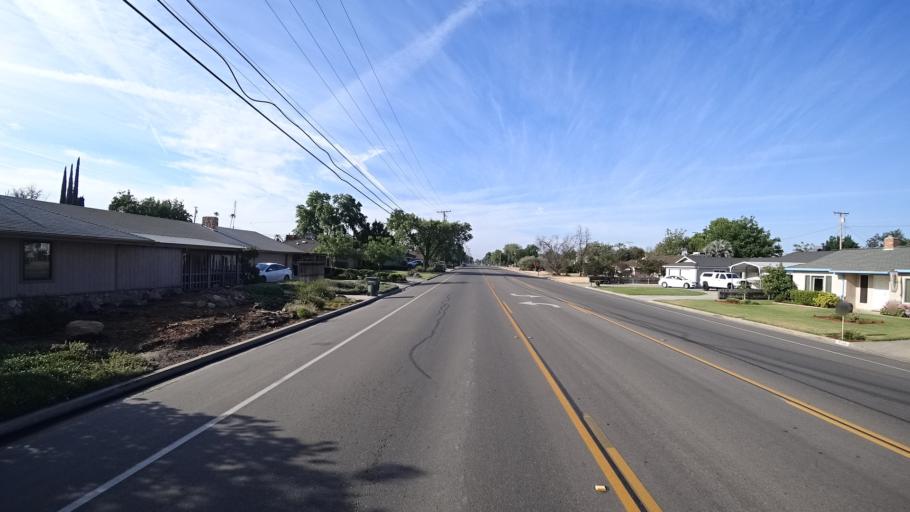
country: US
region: California
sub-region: Kings County
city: Hanford
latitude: 36.3536
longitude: -119.6460
